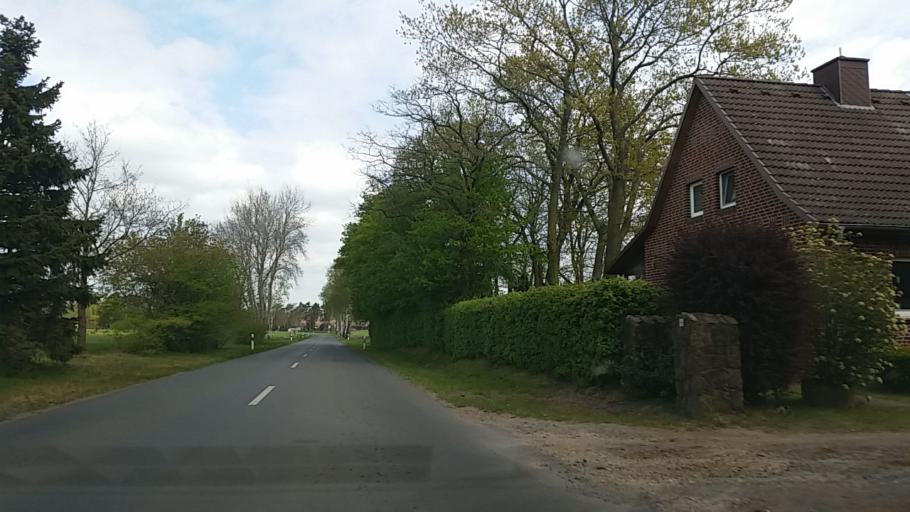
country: DE
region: Lower Saxony
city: Konigsmoor
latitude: 53.2135
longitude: 9.7140
